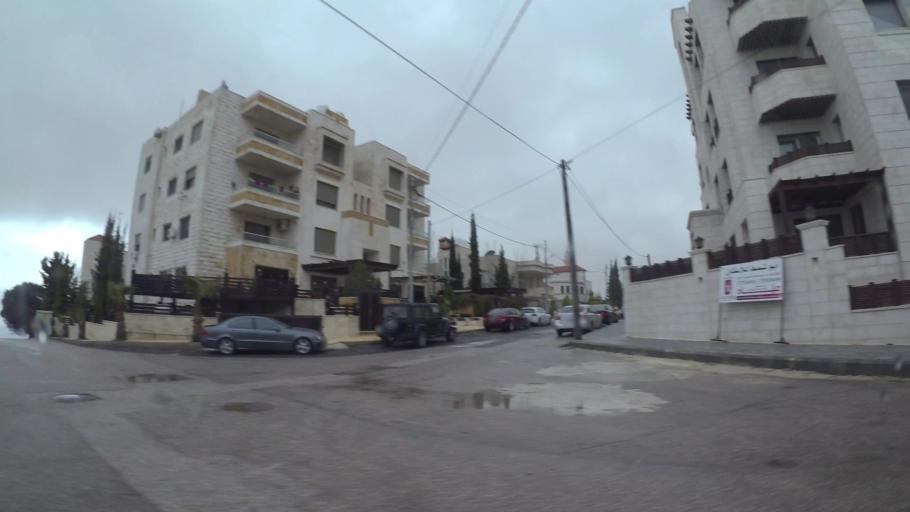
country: JO
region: Amman
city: Al Jubayhah
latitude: 32.0353
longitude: 35.8597
